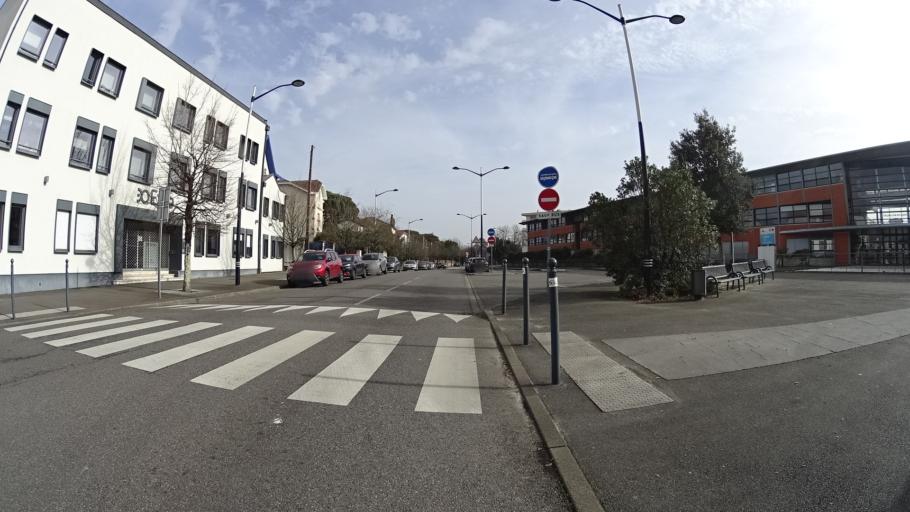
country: FR
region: Aquitaine
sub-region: Departement des Landes
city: Dax
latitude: 43.7054
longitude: -1.0586
